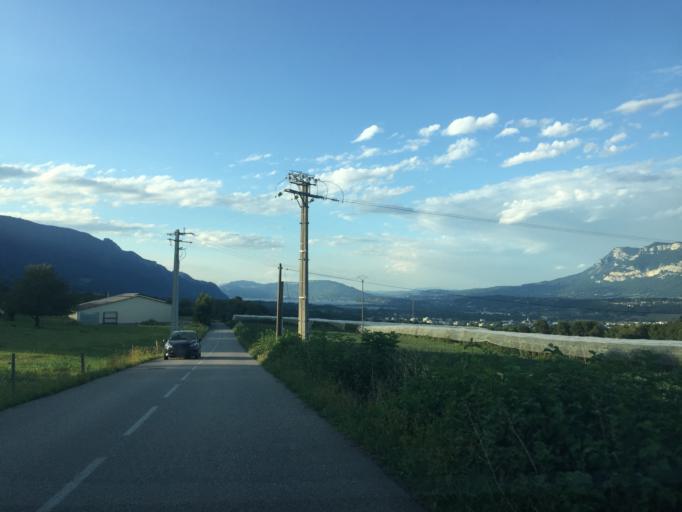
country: FR
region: Rhone-Alpes
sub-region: Departement de la Savoie
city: La Motte-Servolex
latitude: 45.5734
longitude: 5.8591
